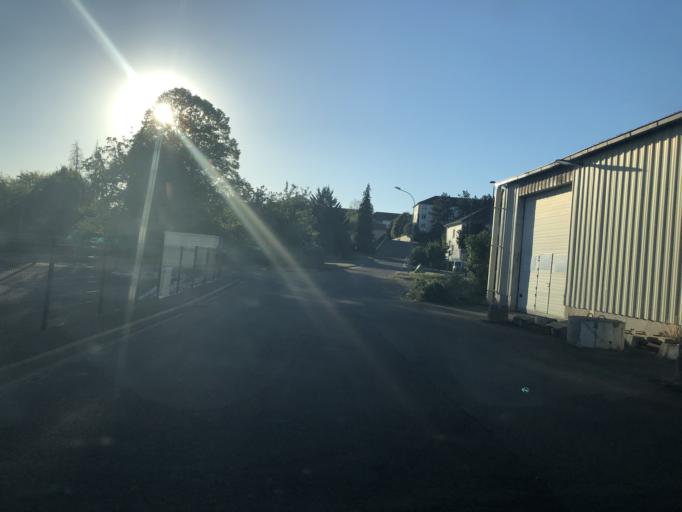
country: FR
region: Bourgogne
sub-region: Departement de l'Yonne
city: Joigny
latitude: 47.9827
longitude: 3.4102
